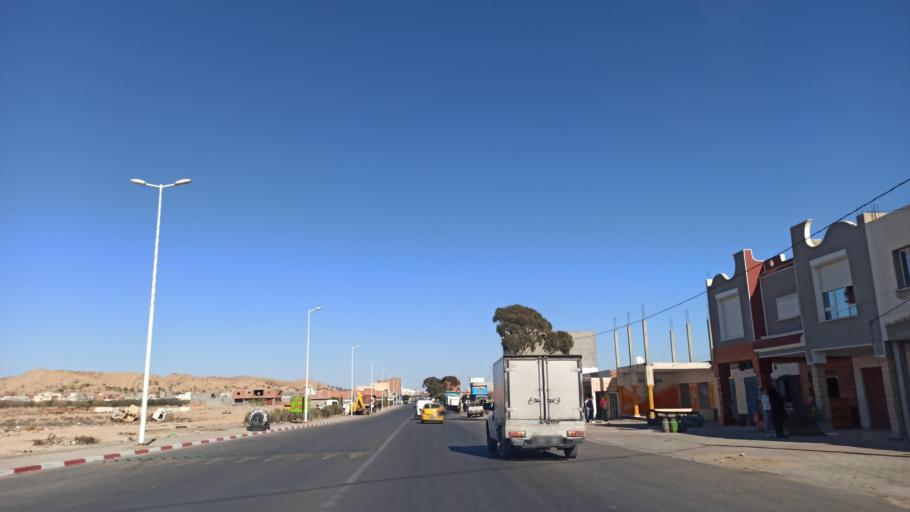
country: TN
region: Sidi Bu Zayd
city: Bi'r al Hufayy
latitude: 34.9169
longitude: 9.1853
